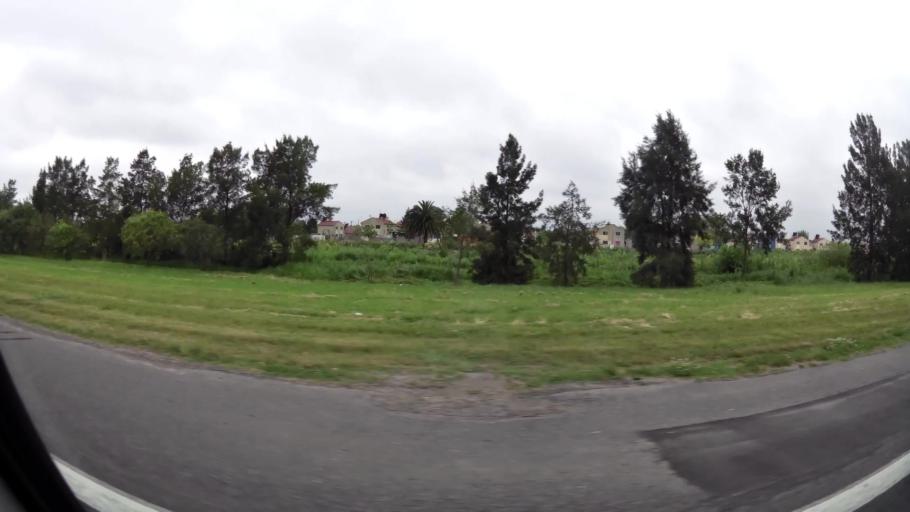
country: AR
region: Buenos Aires
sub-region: Partido de La Plata
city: La Plata
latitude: -34.8748
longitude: -57.9722
